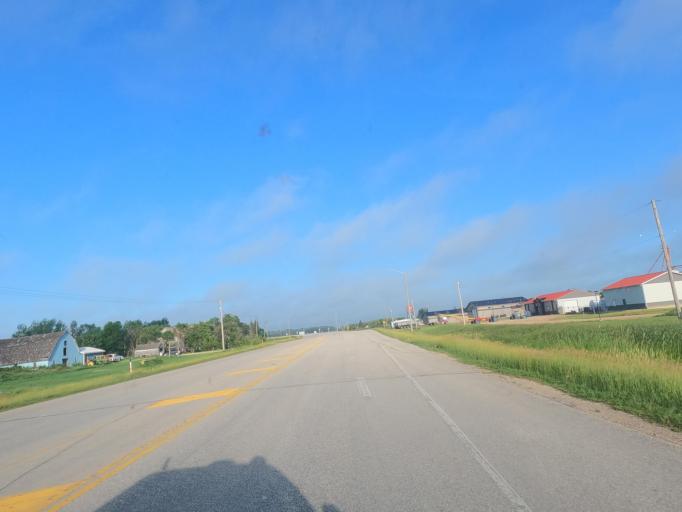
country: CA
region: Manitoba
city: Headingley
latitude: 49.7687
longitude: -97.6147
